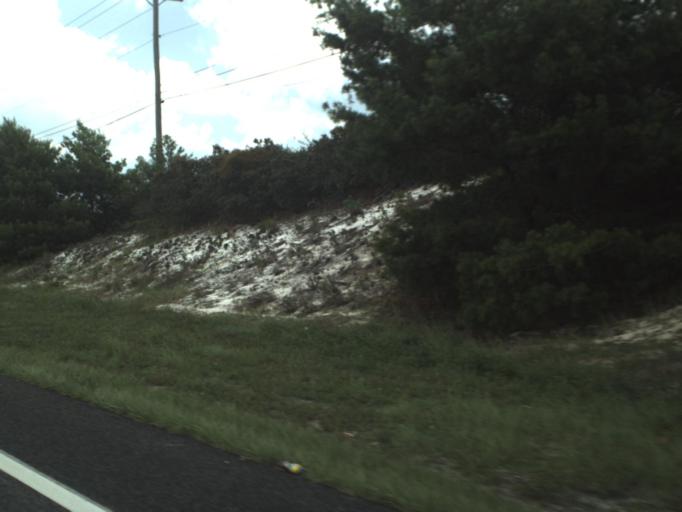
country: US
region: Florida
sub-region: Martin County
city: Hobe Sound
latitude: 27.0201
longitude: -80.1070
